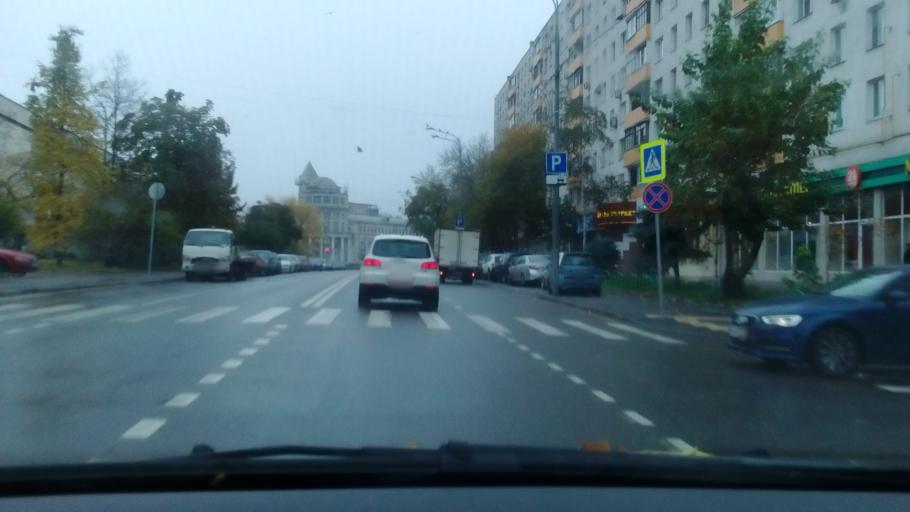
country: RU
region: Moscow
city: Mar'ina Roshcha
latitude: 55.7937
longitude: 37.5769
